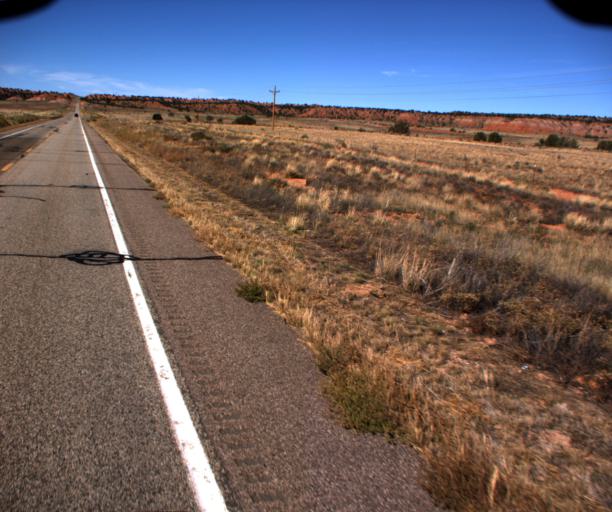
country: US
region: Arizona
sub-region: Mohave County
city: Colorado City
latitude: 36.8756
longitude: -112.8739
